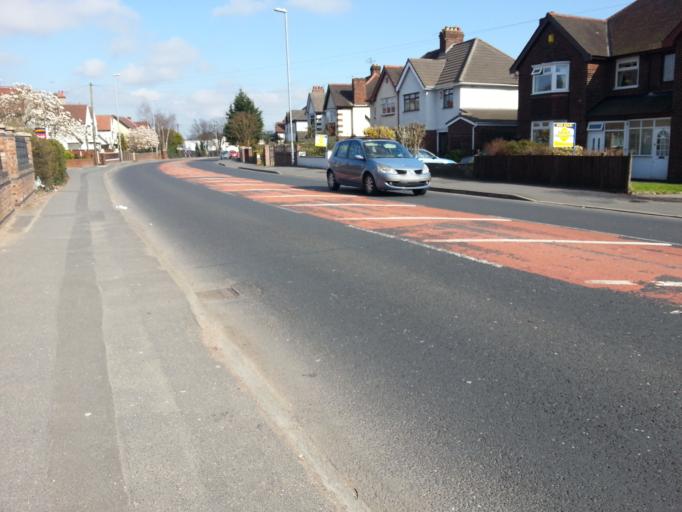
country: GB
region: England
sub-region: Knowsley
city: Huyton
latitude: 53.3611
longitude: -2.8488
